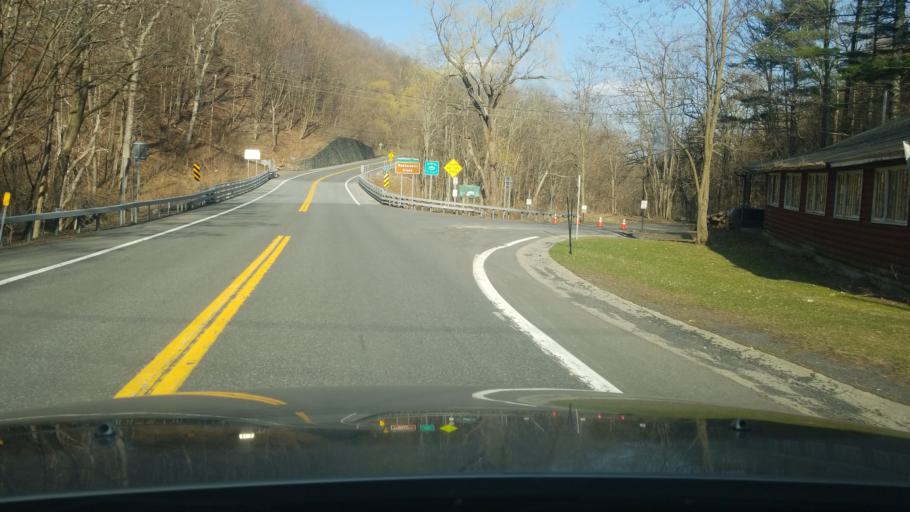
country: US
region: New York
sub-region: Greene County
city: Palenville
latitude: 42.1765
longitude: -74.0378
